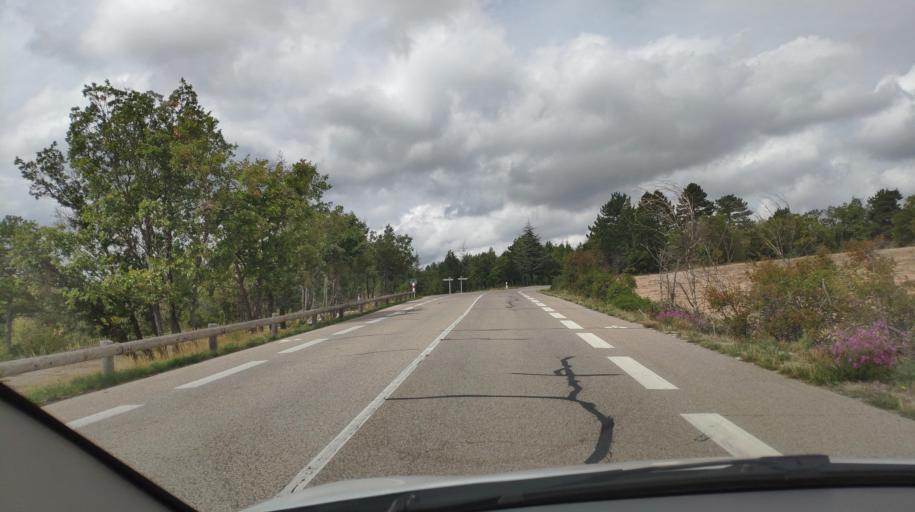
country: FR
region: Provence-Alpes-Cote d'Azur
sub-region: Departement du Vaucluse
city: Sault
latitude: 44.0717
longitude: 5.3536
